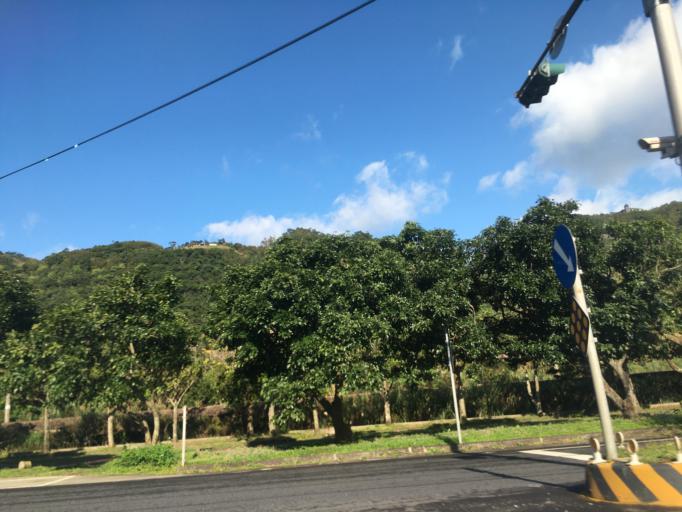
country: TW
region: Taiwan
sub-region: Yilan
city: Yilan
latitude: 24.8770
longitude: 121.8401
